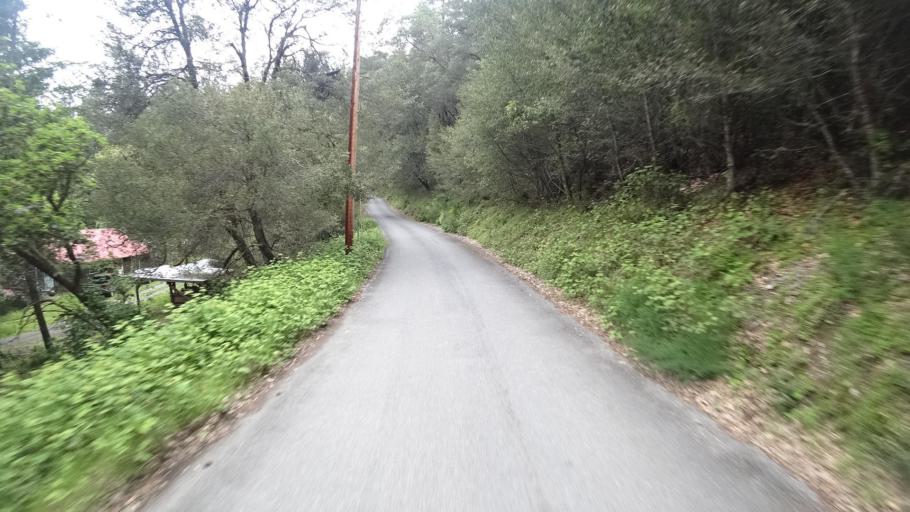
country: US
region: California
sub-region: Humboldt County
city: Willow Creek
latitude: 40.9317
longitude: -123.6154
